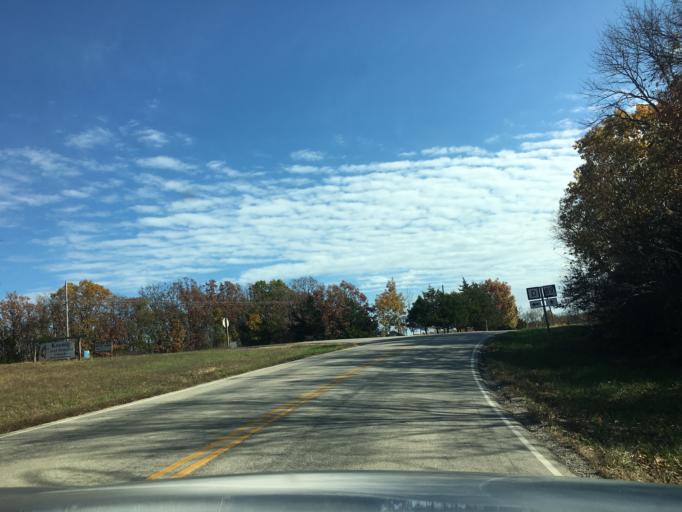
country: US
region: Missouri
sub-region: Maries County
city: Belle
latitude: 38.3369
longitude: -91.7638
